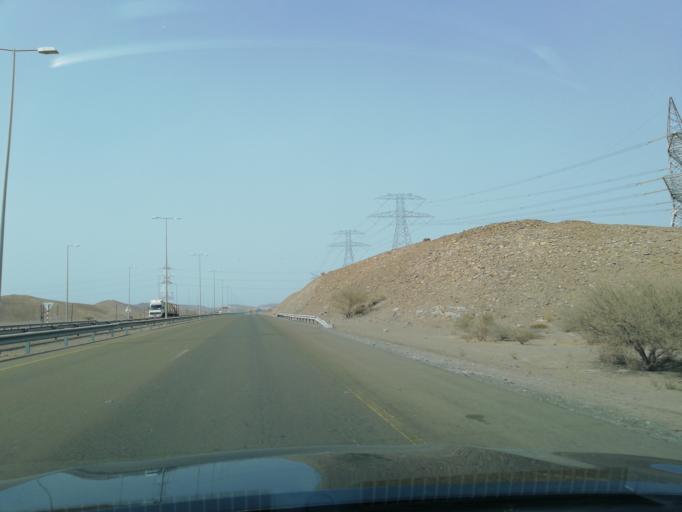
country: OM
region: Al Batinah
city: Al Liwa'
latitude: 24.3529
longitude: 56.5230
